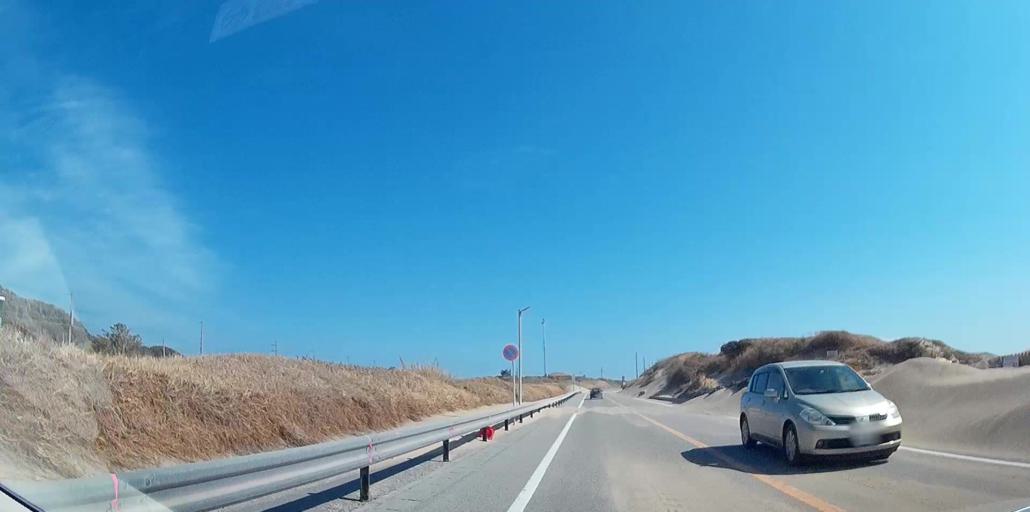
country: JP
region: Chiba
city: Tateyama
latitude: 34.9073
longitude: 139.8356
